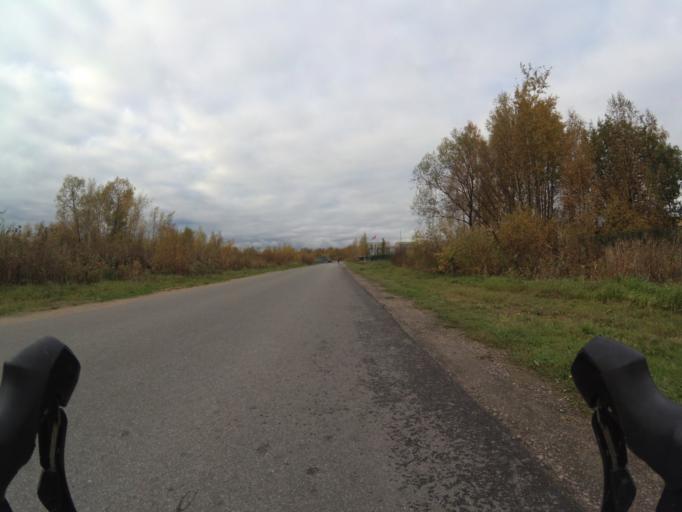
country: RU
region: St.-Petersburg
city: Lakhtinskiy
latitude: 60.0030
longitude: 30.1536
